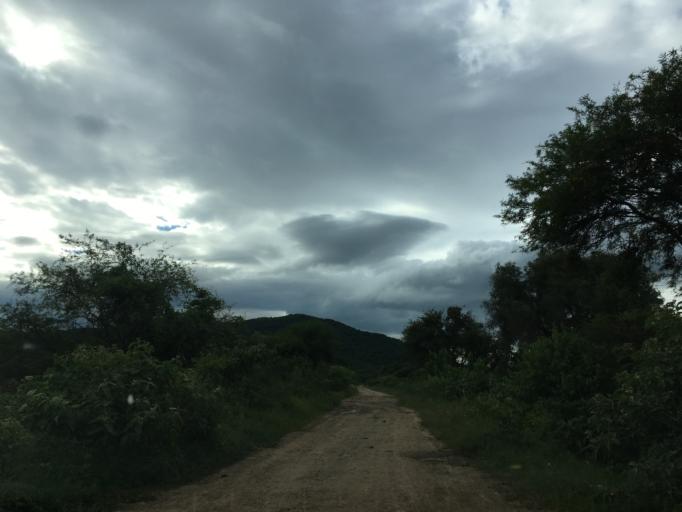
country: MX
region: Guanajuato
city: Iramuco
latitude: 19.9769
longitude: -100.9612
